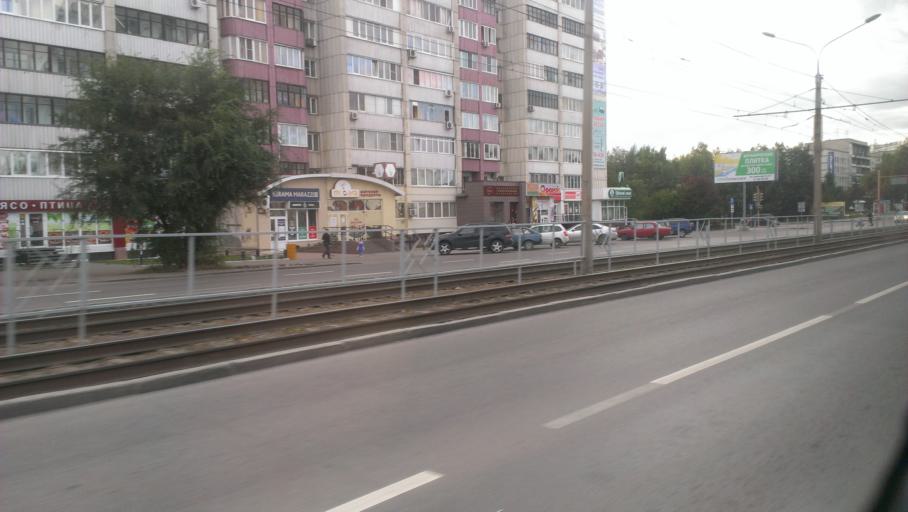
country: RU
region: Altai Krai
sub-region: Gorod Barnaulskiy
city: Barnaul
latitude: 53.3441
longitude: 83.7675
